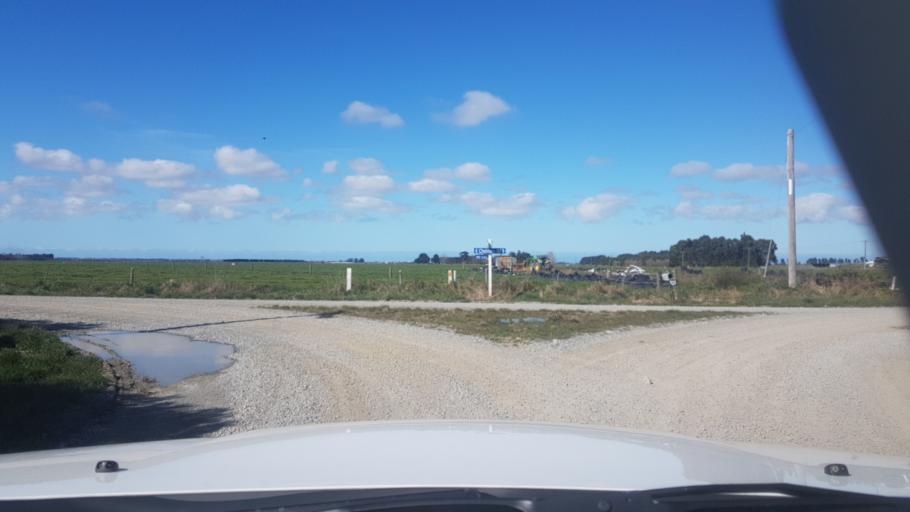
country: NZ
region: Canterbury
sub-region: Timaru District
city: Pleasant Point
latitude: -44.0996
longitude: 171.3901
